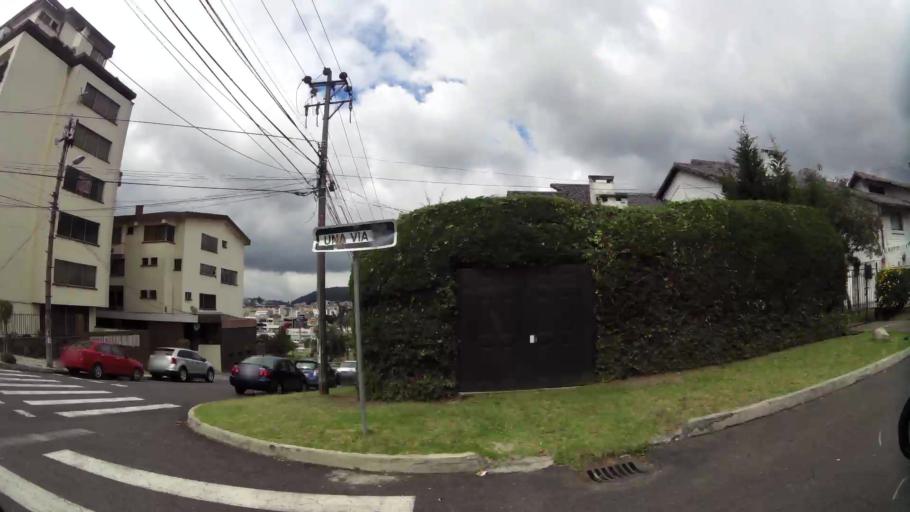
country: EC
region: Pichincha
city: Quito
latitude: -0.1675
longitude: -78.4880
